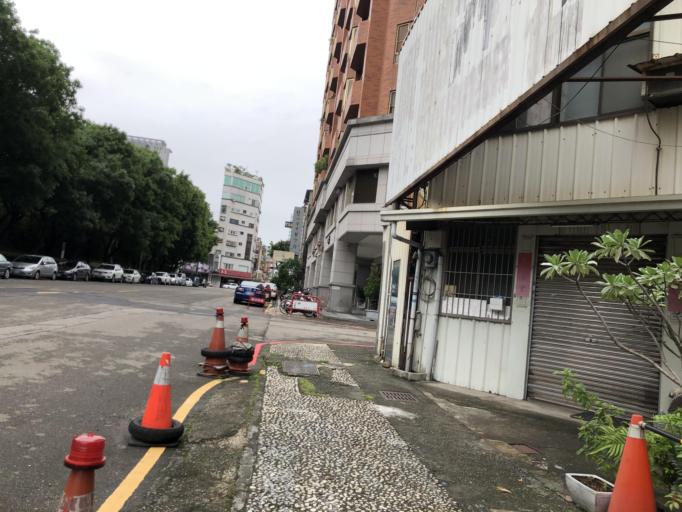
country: TW
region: Taiwan
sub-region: Taichung City
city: Taichung
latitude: 24.1580
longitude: 120.6690
